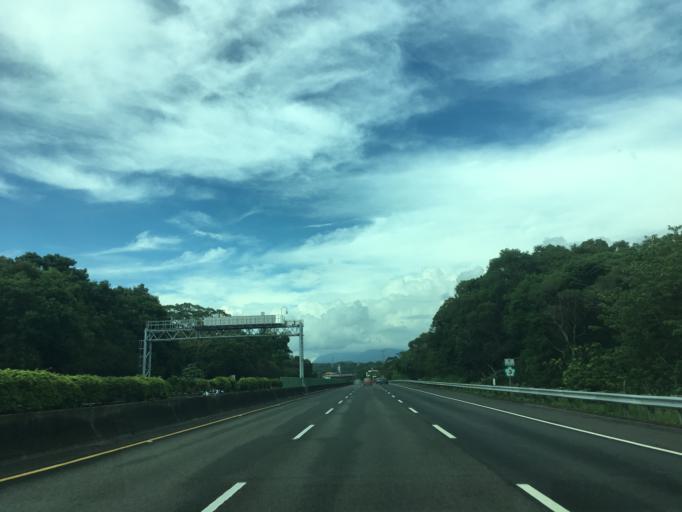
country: TW
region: Taiwan
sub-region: Chiayi
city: Jiayi Shi
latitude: 23.4577
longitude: 120.4906
